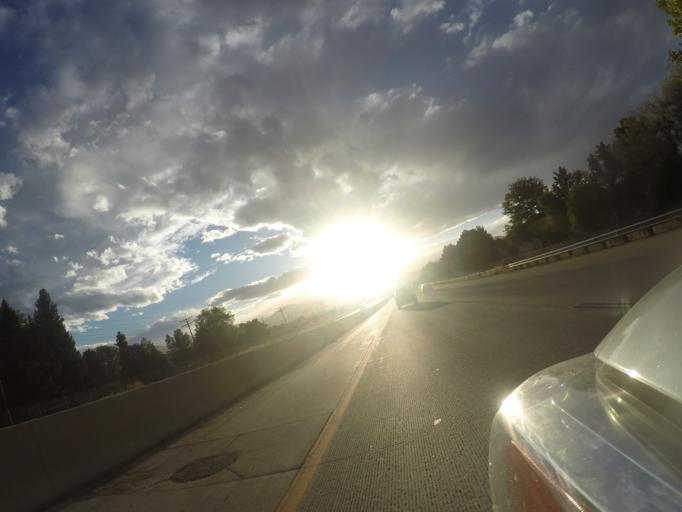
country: US
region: Colorado
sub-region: Jefferson County
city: Lakewood
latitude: 39.6535
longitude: -105.0984
